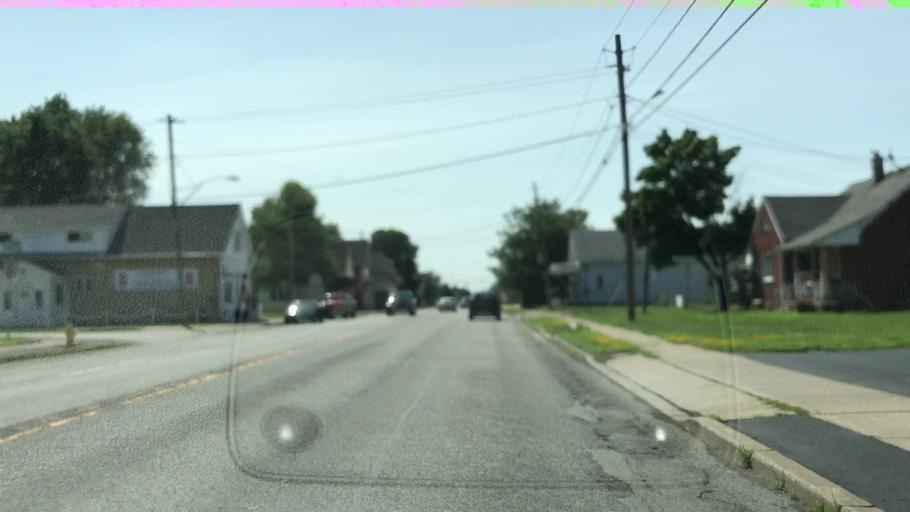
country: US
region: New York
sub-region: Erie County
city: Sloan
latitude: 42.8843
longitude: -78.7787
